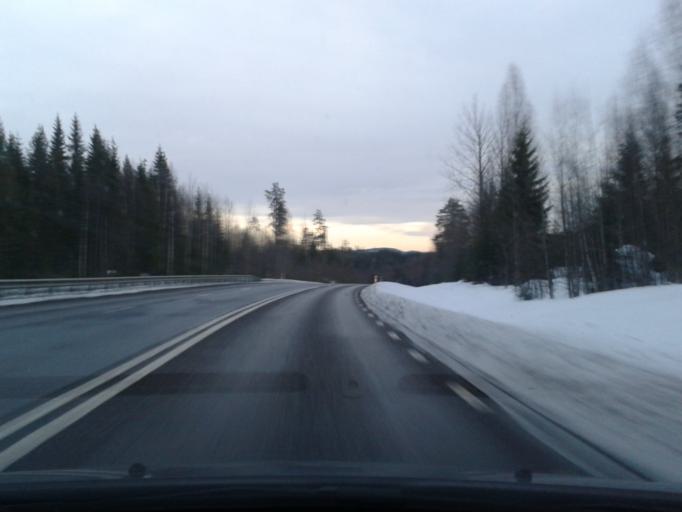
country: SE
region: Vaesternorrland
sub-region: Kramfors Kommun
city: Bollstabruk
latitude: 63.1058
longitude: 17.5082
